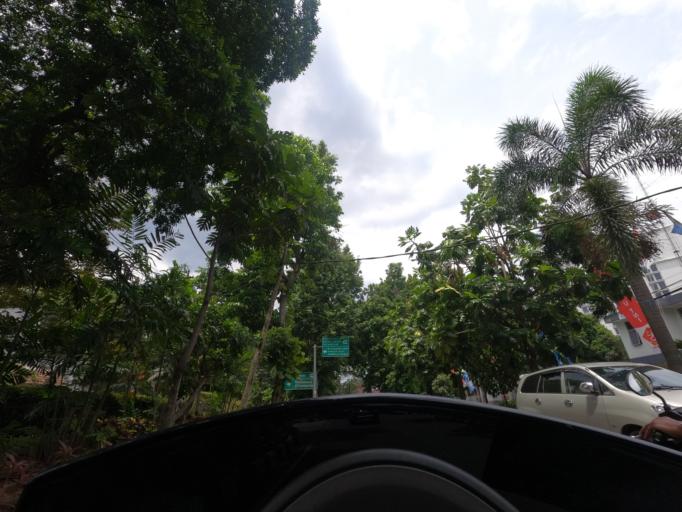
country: ID
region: West Java
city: Bandung
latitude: -6.8999
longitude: 107.6158
